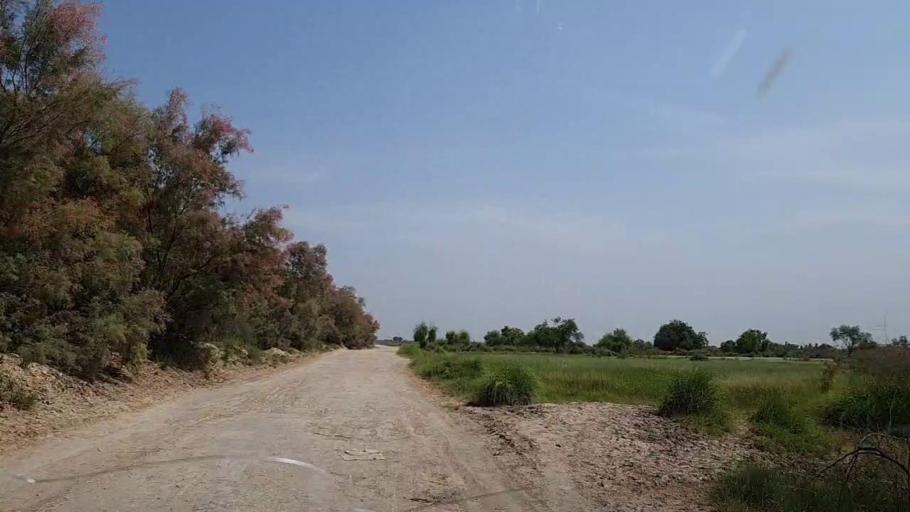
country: PK
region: Sindh
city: Khanpur
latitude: 27.8118
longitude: 69.3080
